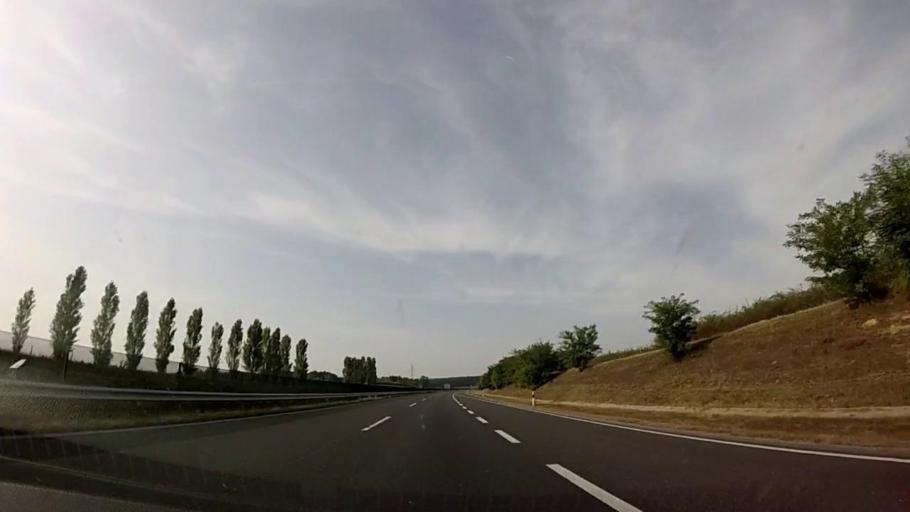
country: HU
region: Somogy
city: Balatonbereny
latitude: 46.6695
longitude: 17.3465
